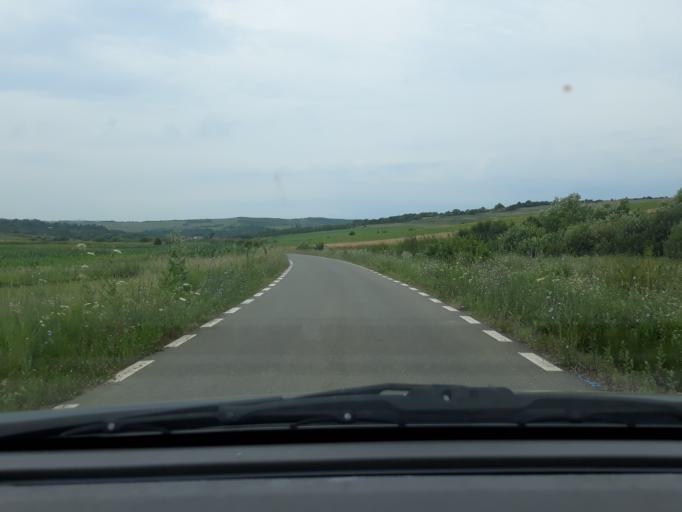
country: RO
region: Salaj
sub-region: Comuna Criseni
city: Criseni
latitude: 47.2724
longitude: 23.0709
